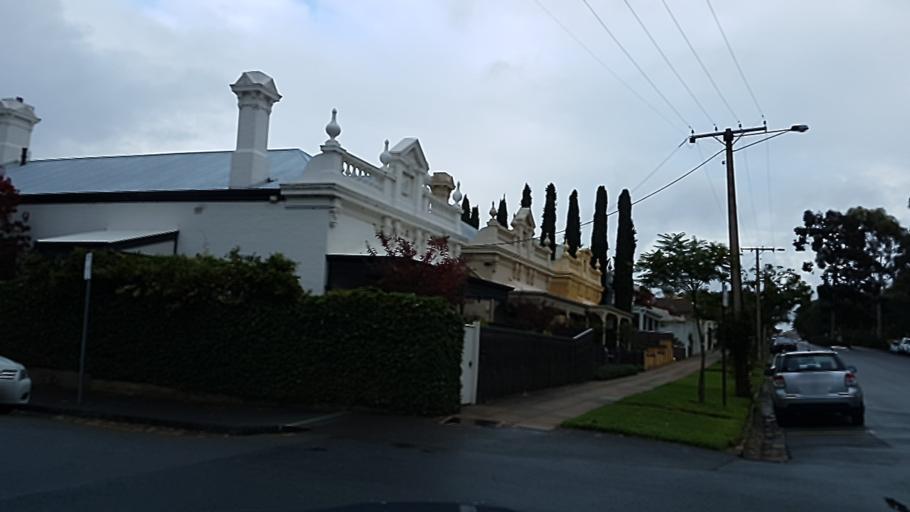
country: AU
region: South Australia
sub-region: Adelaide
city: North Adelaide
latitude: -34.9052
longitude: 138.6057
